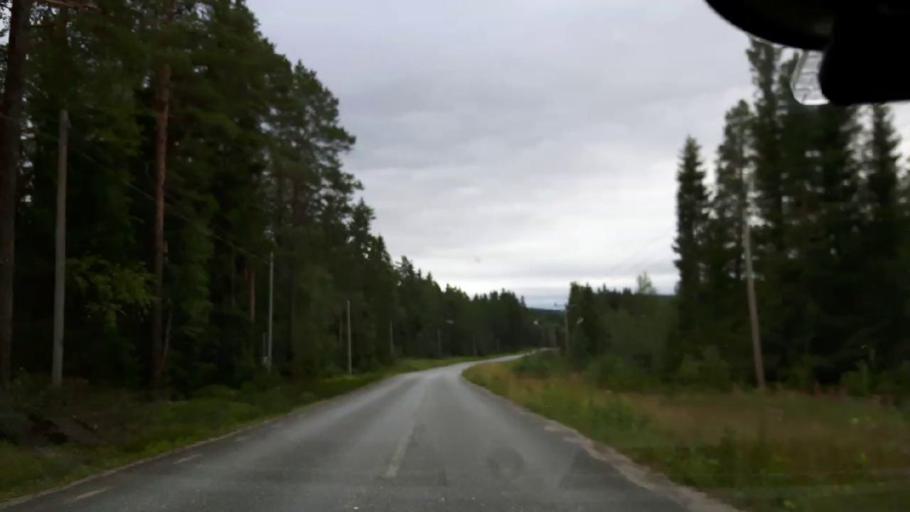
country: SE
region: Jaemtland
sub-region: Braecke Kommun
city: Braecke
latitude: 62.8766
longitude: 15.6175
